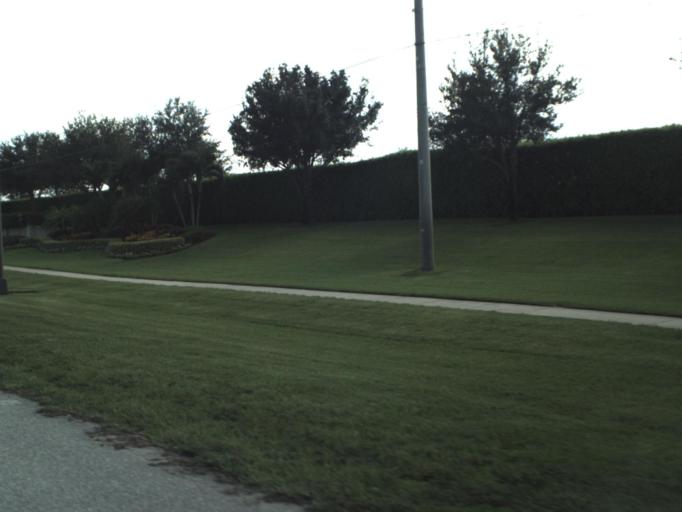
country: US
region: Florida
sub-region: Palm Beach County
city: Boca Pointe
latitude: 26.3631
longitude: -80.2036
